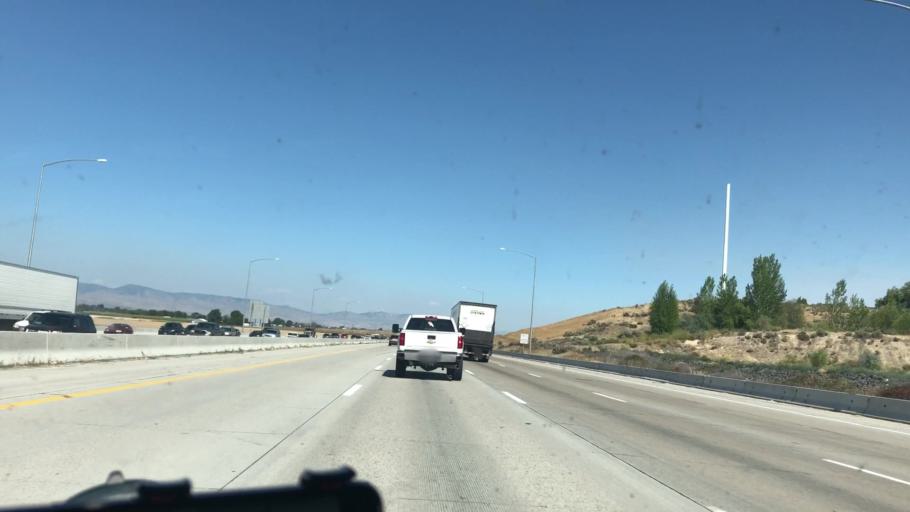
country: US
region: Idaho
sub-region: Canyon County
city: Nampa
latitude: 43.5995
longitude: -116.5065
